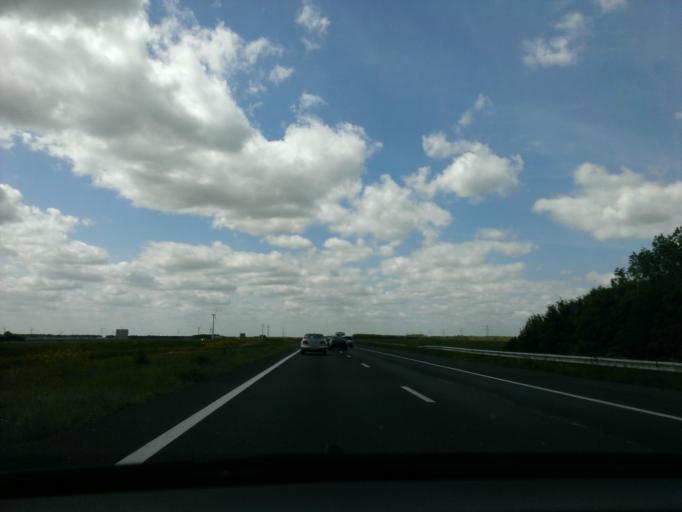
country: NL
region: Flevoland
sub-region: Gemeente Lelystad
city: Lelystad
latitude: 52.4226
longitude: 5.4013
